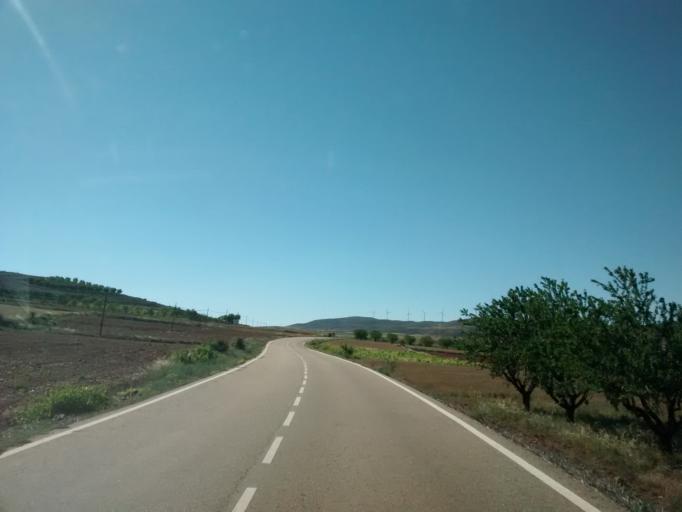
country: ES
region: Aragon
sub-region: Provincia de Zaragoza
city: Trasmoz
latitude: 41.8402
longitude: -1.7154
